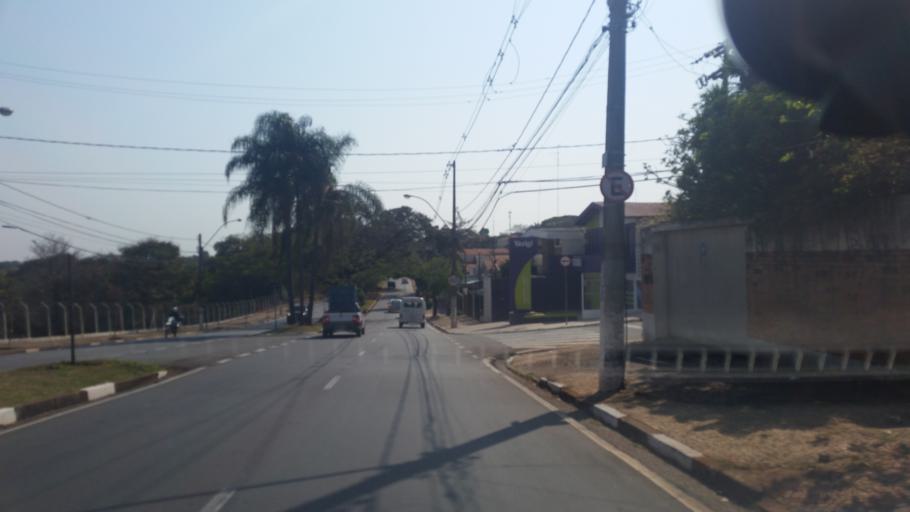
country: BR
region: Sao Paulo
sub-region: Campinas
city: Campinas
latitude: -22.8863
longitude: -47.0782
